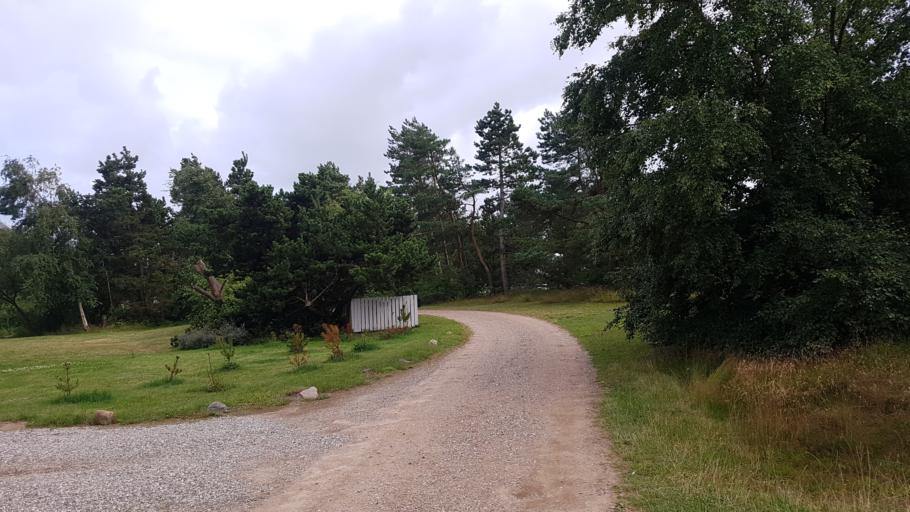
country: DE
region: Schleswig-Holstein
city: List
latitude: 55.0863
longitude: 8.5306
